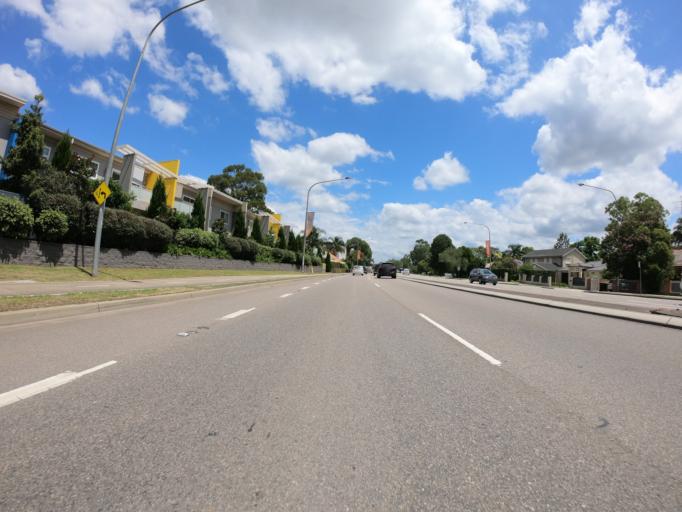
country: AU
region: New South Wales
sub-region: Penrith Municipality
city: Penrith
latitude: -33.7614
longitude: 150.6838
